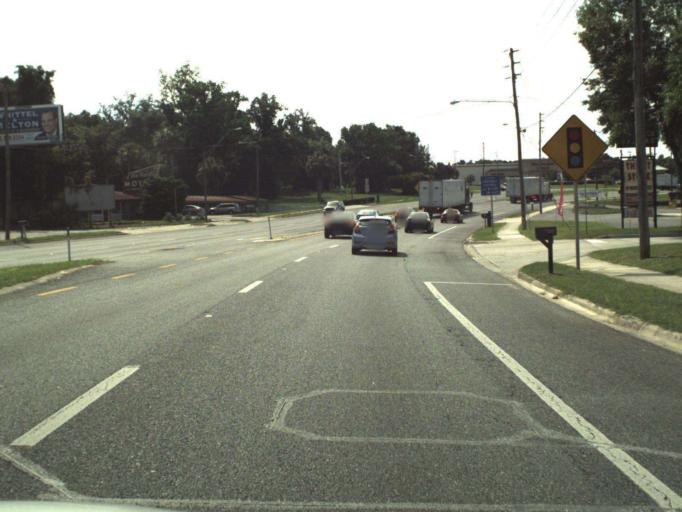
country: US
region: Florida
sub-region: Marion County
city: Belleview
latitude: 29.0609
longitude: -82.0637
